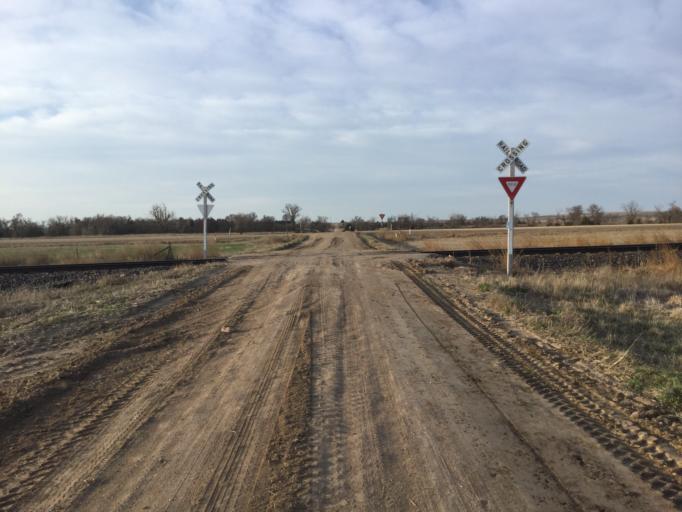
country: US
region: Kansas
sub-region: Ellis County
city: Ellis
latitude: 38.9388
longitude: -99.6135
